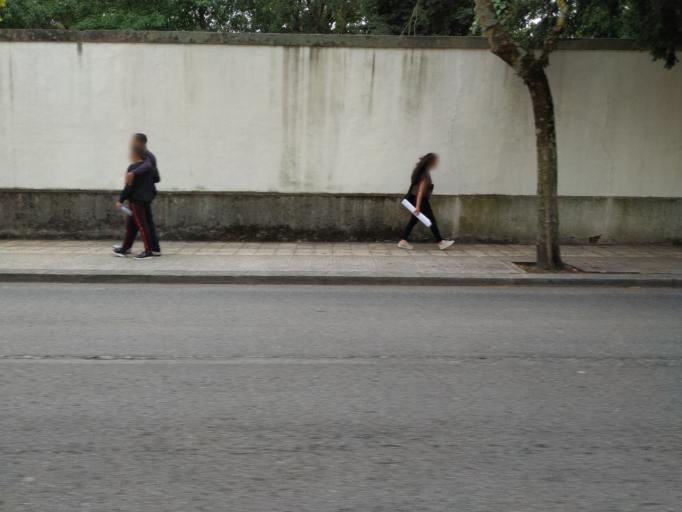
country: PT
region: Porto
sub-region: Porto
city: Porto
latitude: 41.1538
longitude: -8.6415
